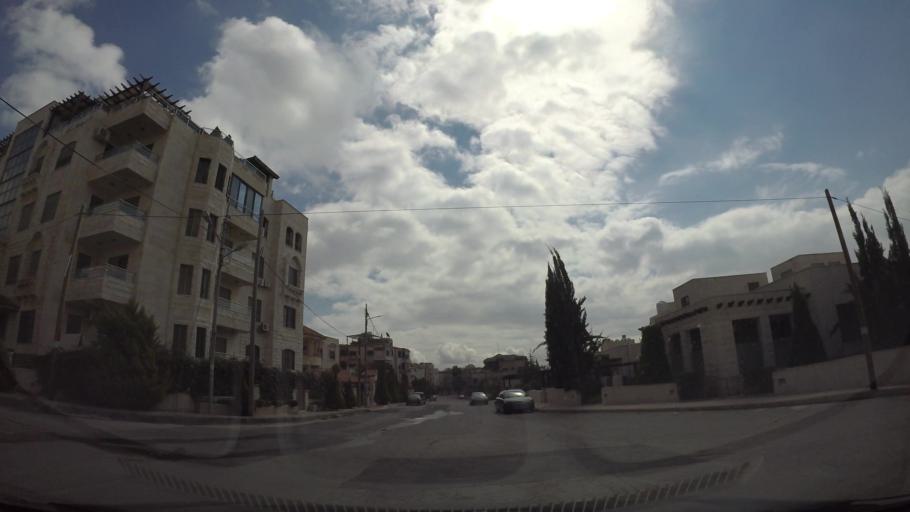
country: JO
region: Amman
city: Wadi as Sir
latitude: 31.9623
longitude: 35.8366
